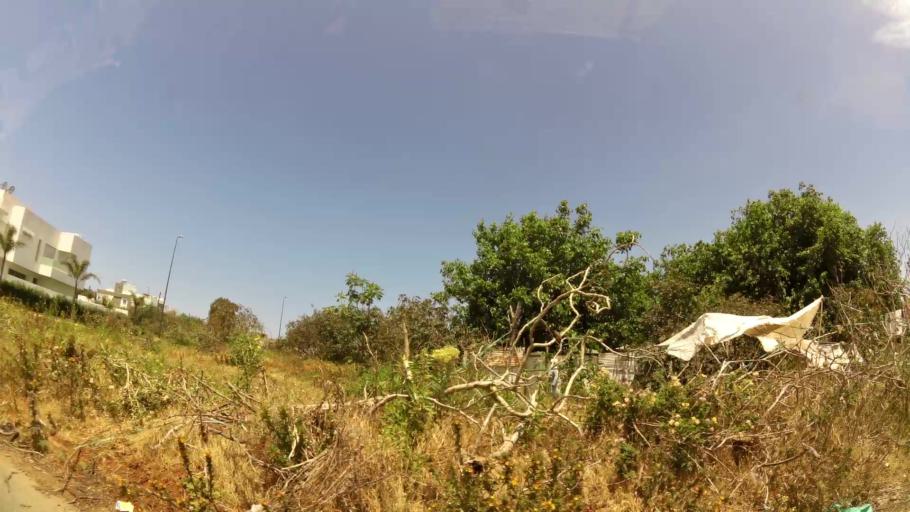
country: MA
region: Gharb-Chrarda-Beni Hssen
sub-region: Kenitra Province
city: Kenitra
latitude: 34.2640
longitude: -6.6283
